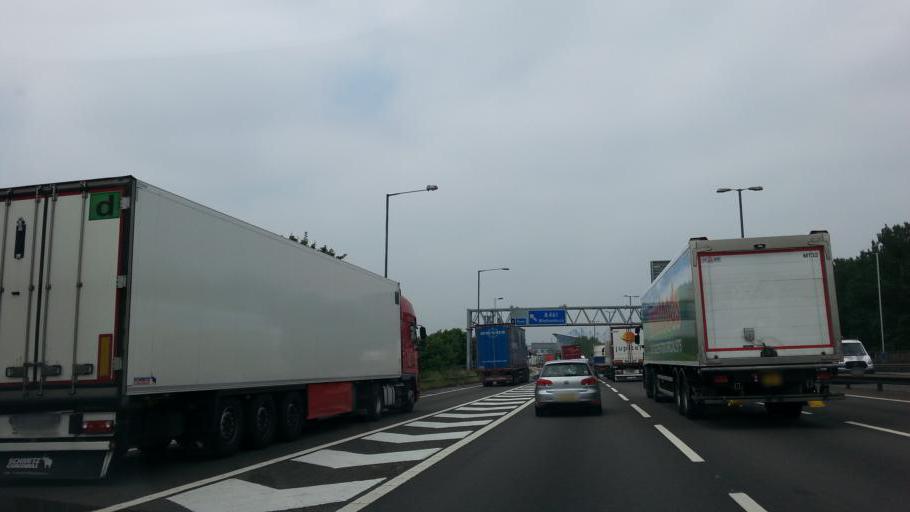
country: GB
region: England
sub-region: Walsall
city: Walsall
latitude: 52.5590
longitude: -1.9796
